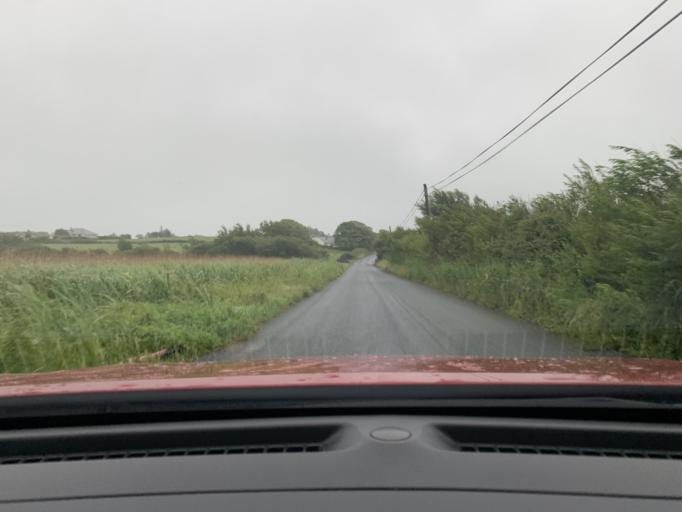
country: IE
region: Connaught
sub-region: County Leitrim
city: Kinlough
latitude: 54.4451
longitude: -8.4425
